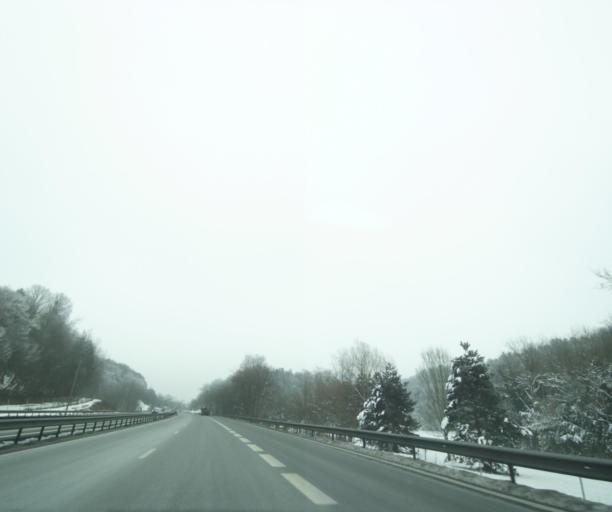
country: FR
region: Rhone-Alpes
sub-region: Departement de l'Ain
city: Poncin
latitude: 46.1030
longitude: 5.4415
